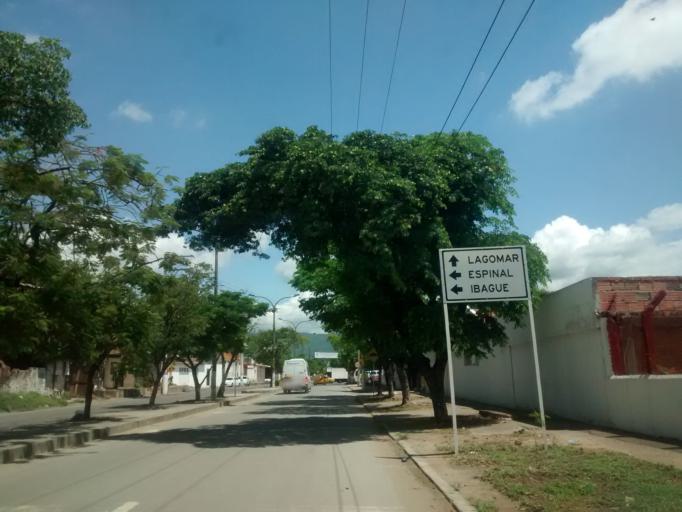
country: CO
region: Cundinamarca
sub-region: Girardot
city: Girardot City
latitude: 4.3020
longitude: -74.7999
